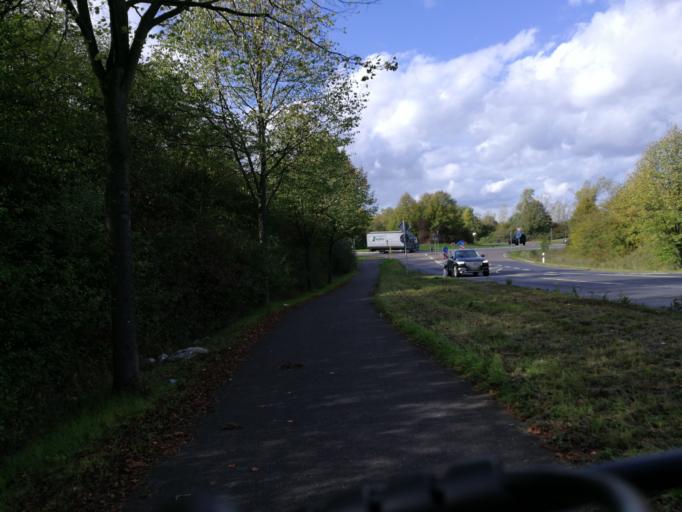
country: DE
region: North Rhine-Westphalia
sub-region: Regierungsbezirk Dusseldorf
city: Dusseldorf
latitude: 51.1467
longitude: 6.7563
